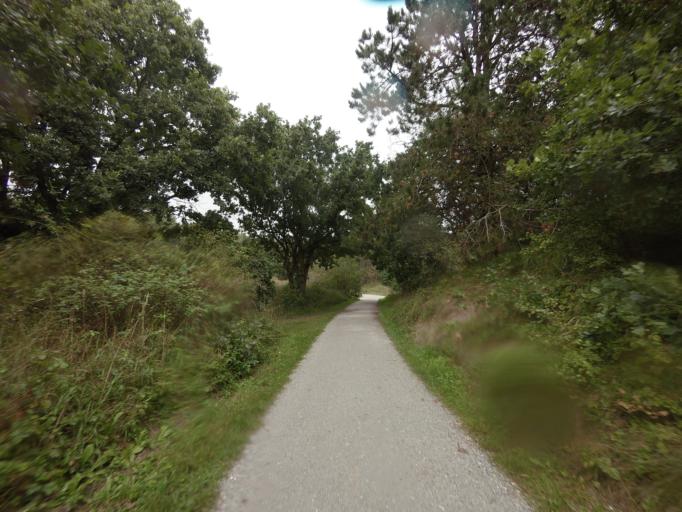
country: NL
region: Friesland
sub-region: Gemeente Schiermonnikoog
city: Schiermonnikoog
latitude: 53.4834
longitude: 6.1634
